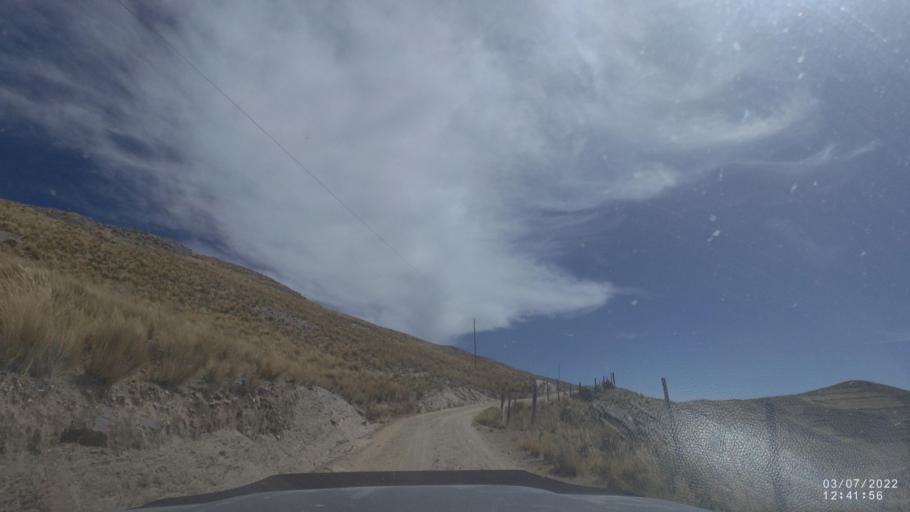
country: BO
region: Cochabamba
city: Irpa Irpa
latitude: -17.7852
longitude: -66.6252
